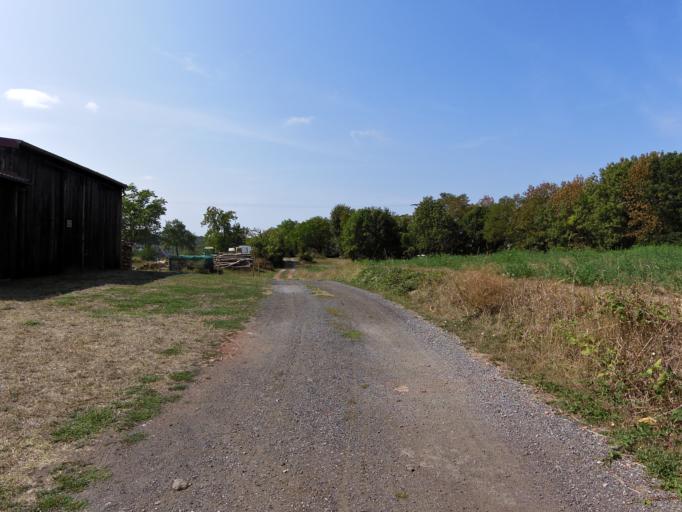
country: DE
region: Bavaria
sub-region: Regierungsbezirk Unterfranken
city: Theilheim
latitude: 49.7567
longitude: 10.0312
